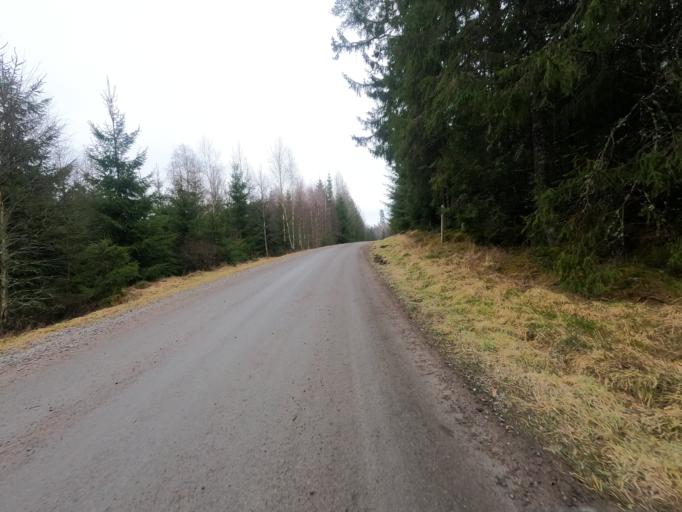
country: SE
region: Kronoberg
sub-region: Markaryds Kommun
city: Stromsnasbruk
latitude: 56.8173
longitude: 13.5649
